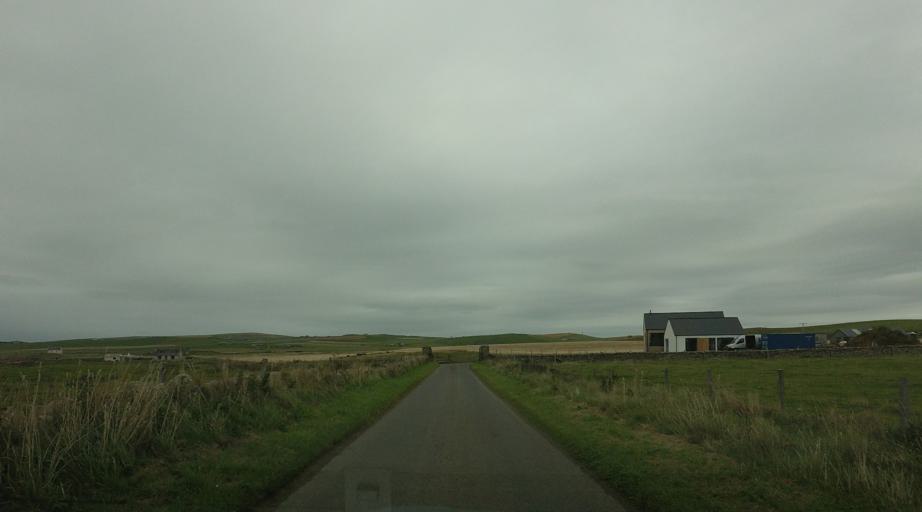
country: GB
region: Scotland
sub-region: Orkney Islands
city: Stromness
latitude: 59.0493
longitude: -3.3333
